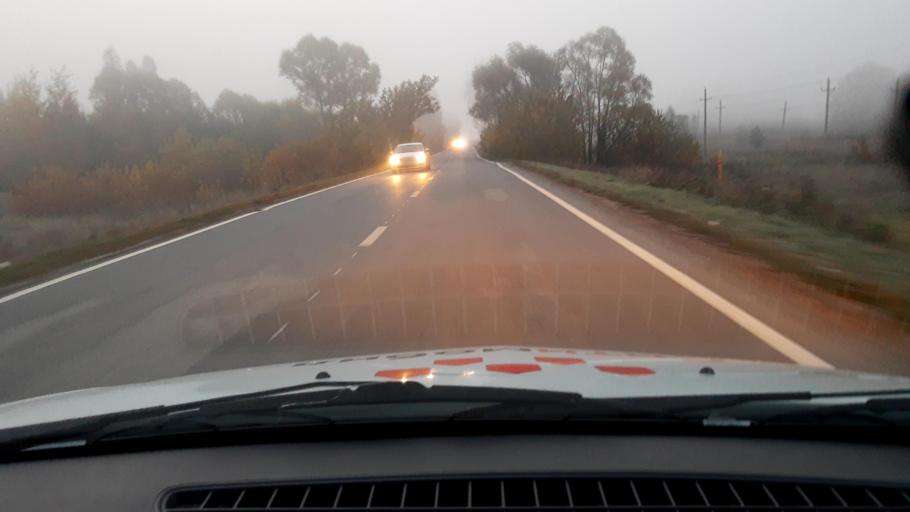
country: RU
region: Bashkortostan
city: Iglino
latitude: 54.7452
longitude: 56.2147
